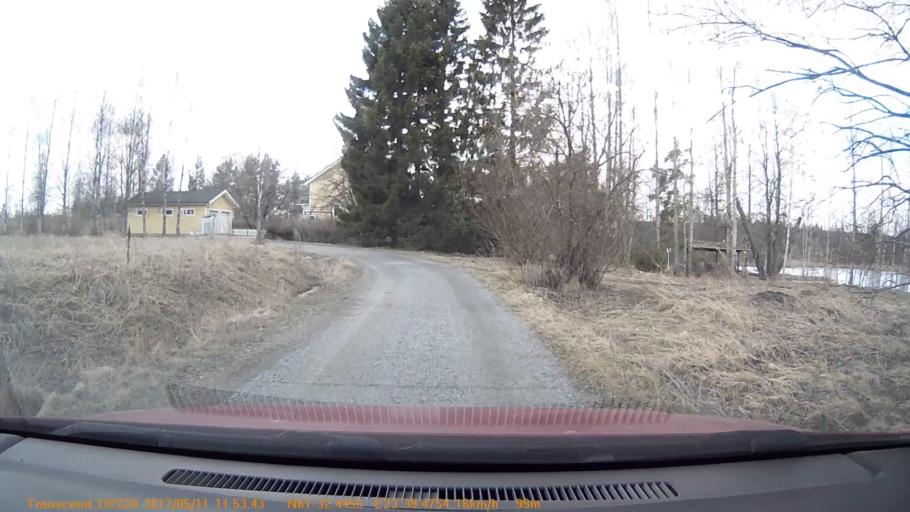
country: FI
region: Pirkanmaa
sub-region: Tampere
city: Yloejaervi
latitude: 61.5408
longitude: 23.6580
